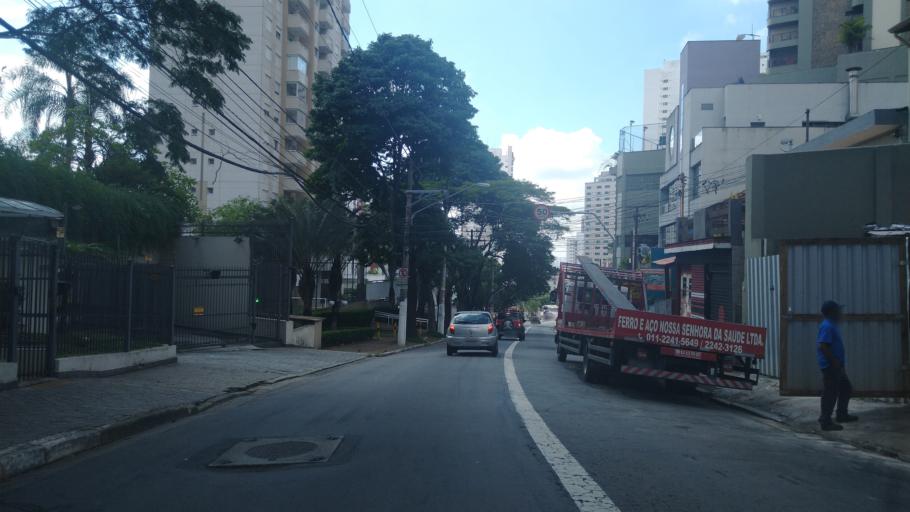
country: BR
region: Sao Paulo
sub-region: Sao Paulo
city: Sao Paulo
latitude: -23.4939
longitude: -46.6251
